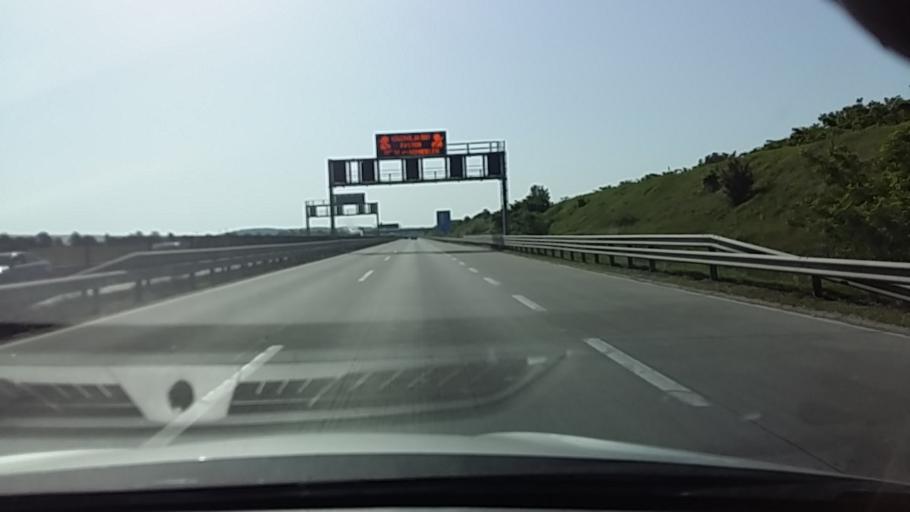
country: HU
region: Budapest
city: Budapest XVI. keruelet
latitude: 47.5479
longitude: 19.1916
